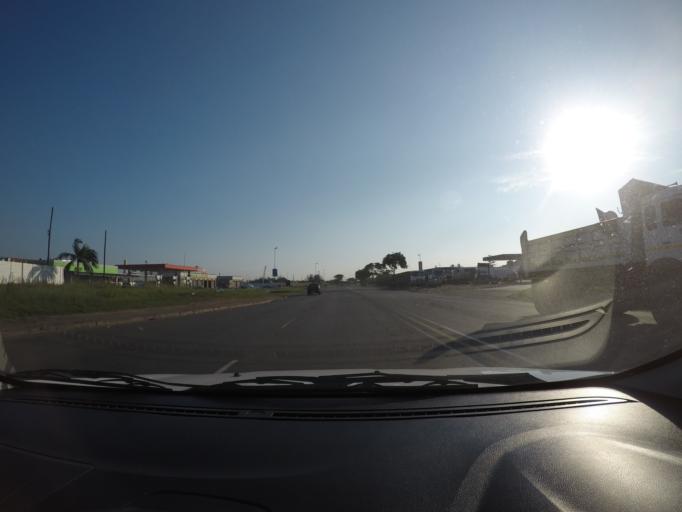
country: ZA
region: KwaZulu-Natal
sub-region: uThungulu District Municipality
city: Richards Bay
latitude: -28.7596
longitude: 32.0237
